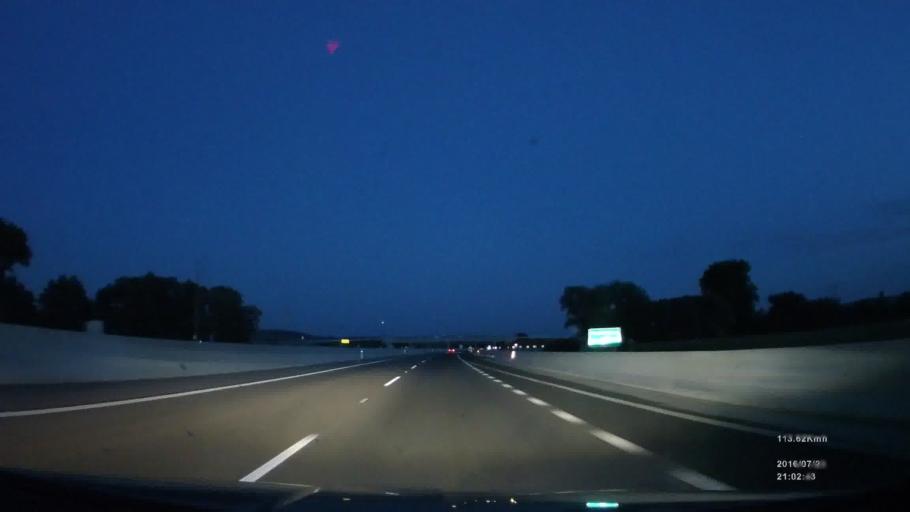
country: SK
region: Kosicky
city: Kosice
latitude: 48.8331
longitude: 21.3058
